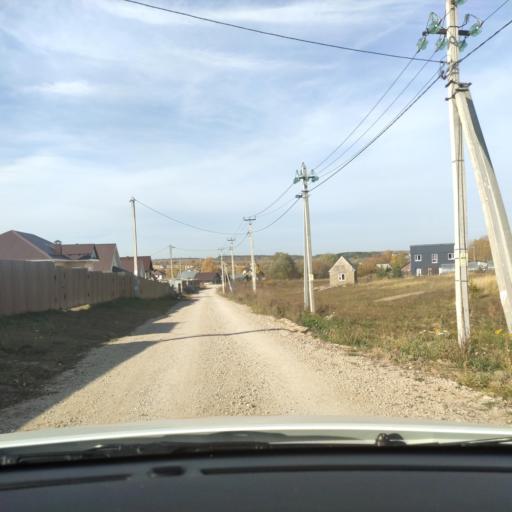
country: RU
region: Tatarstan
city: Vysokaya Gora
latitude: 55.7475
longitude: 49.4078
